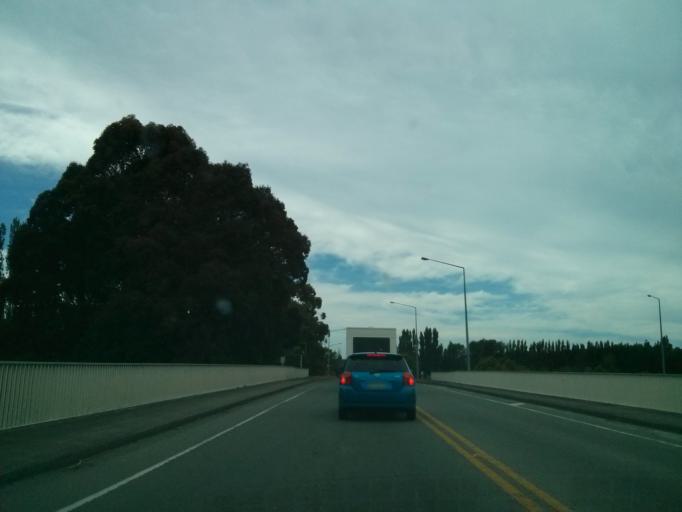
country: NZ
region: Canterbury
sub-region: Waimakariri District
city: Kaiapoi
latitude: -43.4080
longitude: 172.6443
